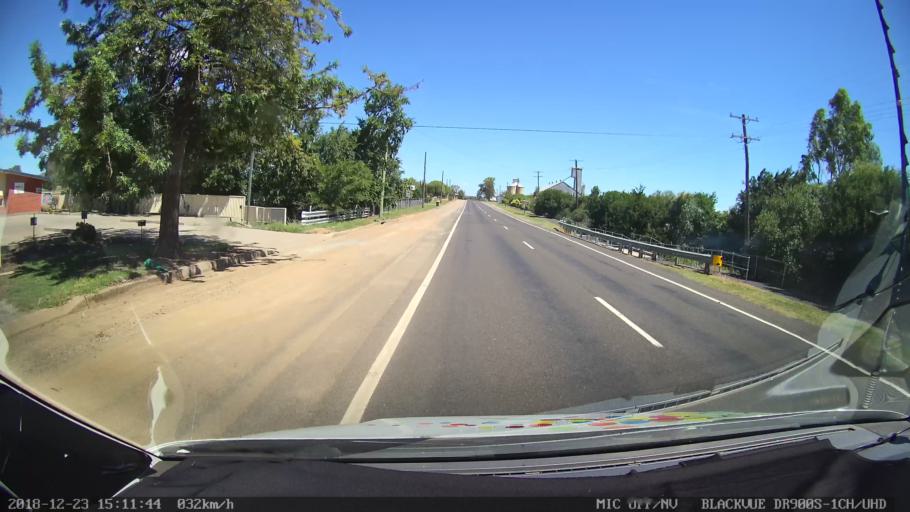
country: AU
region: New South Wales
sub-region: Tamworth Municipality
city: Manilla
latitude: -30.7506
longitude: 150.7259
